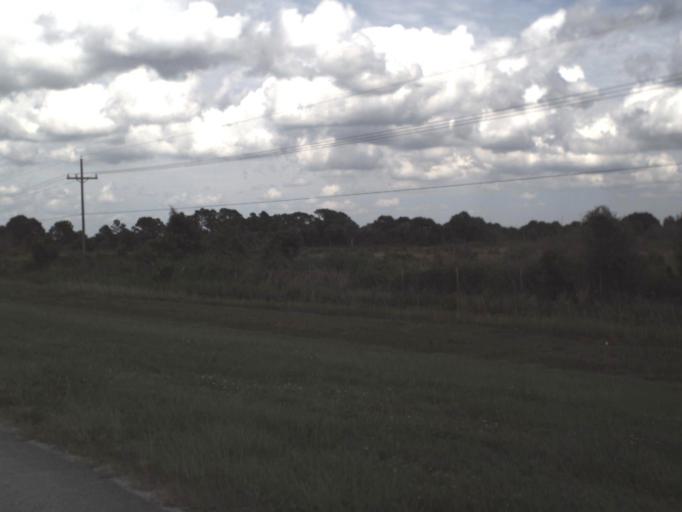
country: US
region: Florida
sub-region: Hendry County
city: Port LaBelle
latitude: 26.6382
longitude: -81.4363
